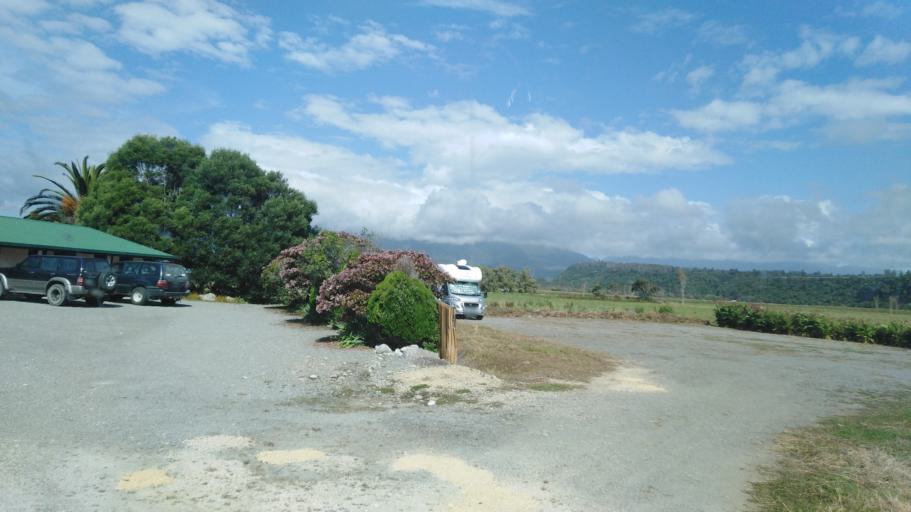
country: NZ
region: West Coast
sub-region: Buller District
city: Westport
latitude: -41.2485
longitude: 172.1115
